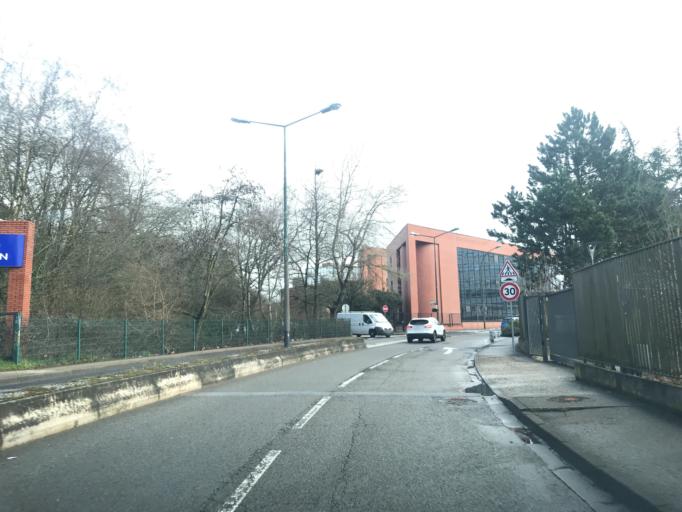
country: FR
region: Ile-de-France
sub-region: Departement des Yvelines
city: Velizy-Villacoublay
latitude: 48.7873
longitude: 2.2090
